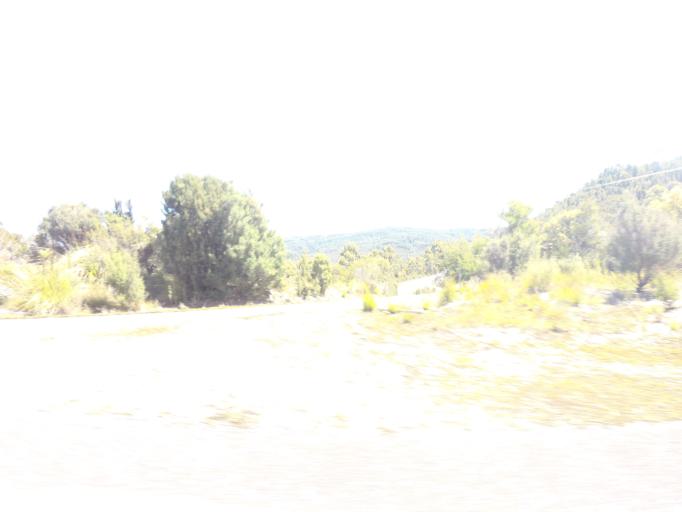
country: AU
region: Tasmania
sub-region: West Coast
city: Queenstown
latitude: -42.7826
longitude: 146.0325
